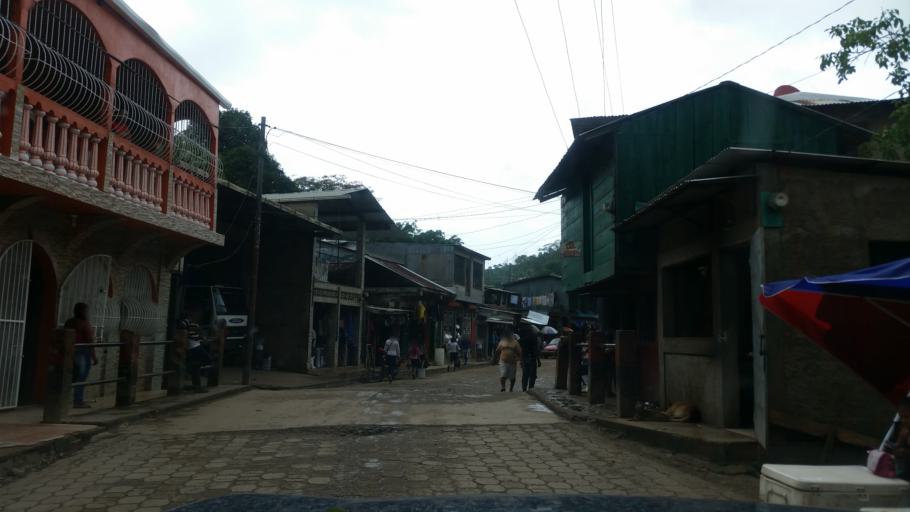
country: NI
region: Atlantico Norte (RAAN)
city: Bonanza
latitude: 14.0293
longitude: -84.5978
